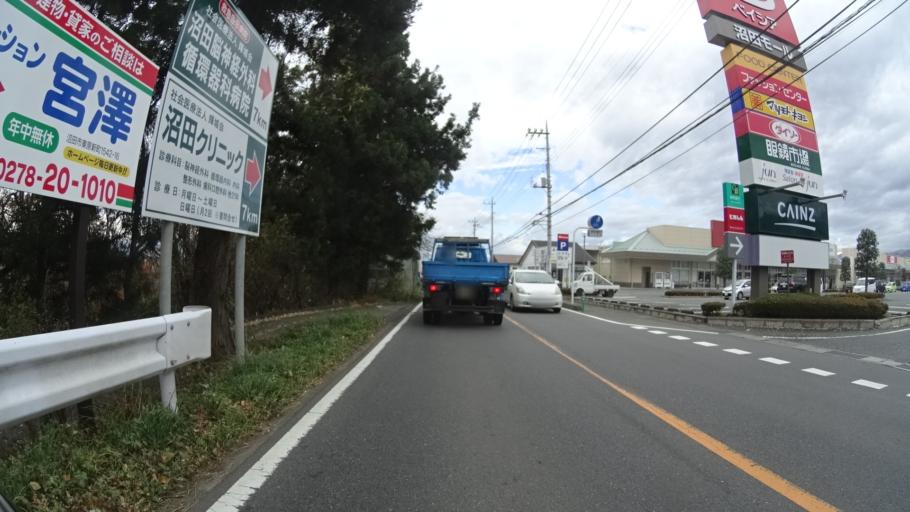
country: JP
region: Gunma
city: Numata
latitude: 36.6646
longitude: 139.1088
